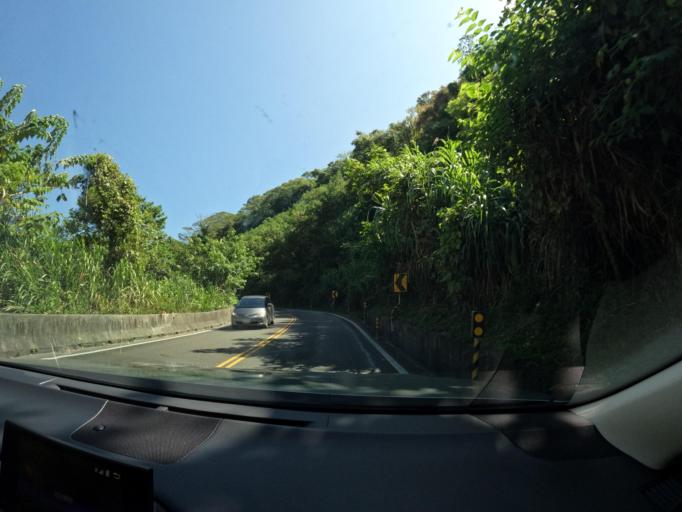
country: TW
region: Taiwan
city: Yujing
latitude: 23.1963
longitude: 120.7943
